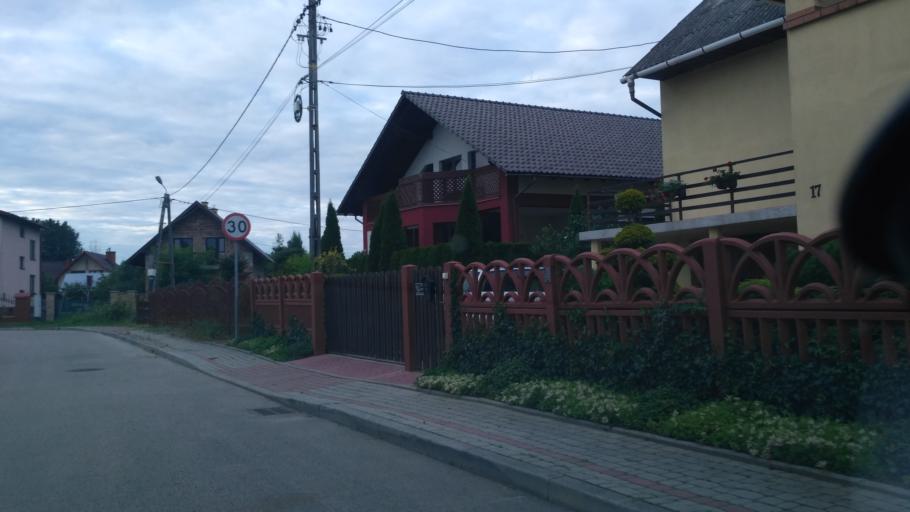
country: PL
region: Subcarpathian Voivodeship
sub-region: Powiat ropczycko-sedziszowski
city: Sedziszow Malopolski
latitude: 50.0784
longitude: 21.6968
